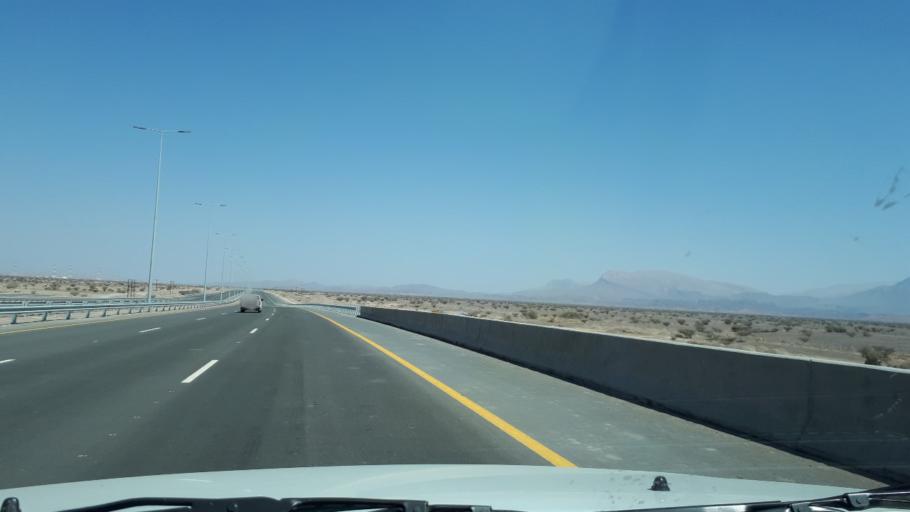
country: OM
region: Ash Sharqiyah
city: Badiyah
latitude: 22.3611
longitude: 59.1117
